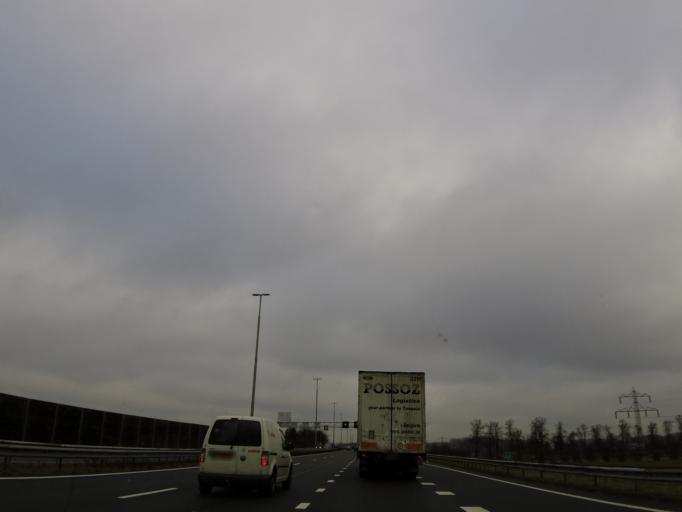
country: NL
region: Limburg
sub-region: Gemeente Sittard-Geleen
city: Born
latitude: 51.0444
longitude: 5.8263
